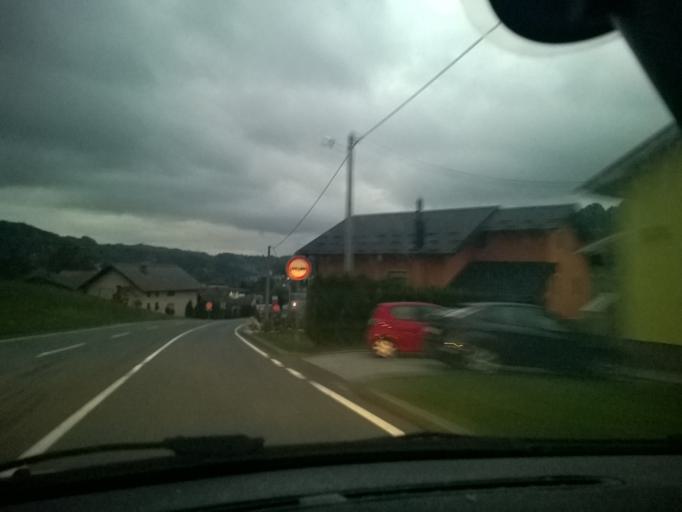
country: HR
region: Krapinsko-Zagorska
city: Pregrada
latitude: 46.2084
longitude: 15.7725
